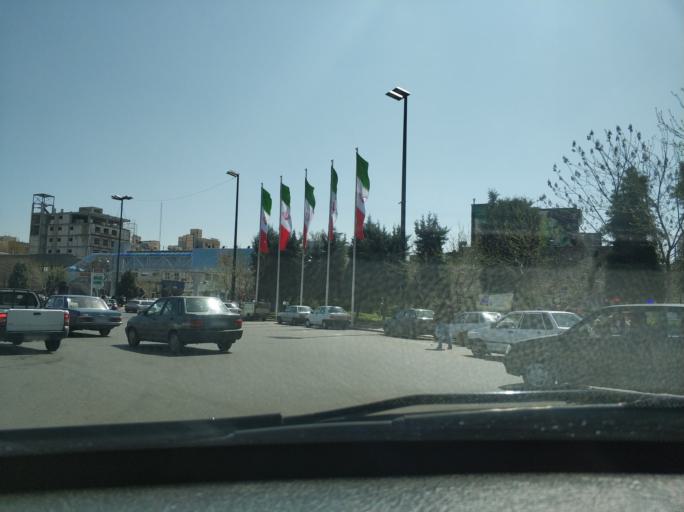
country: IR
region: Razavi Khorasan
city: Mashhad
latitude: 36.2676
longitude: 59.5984
